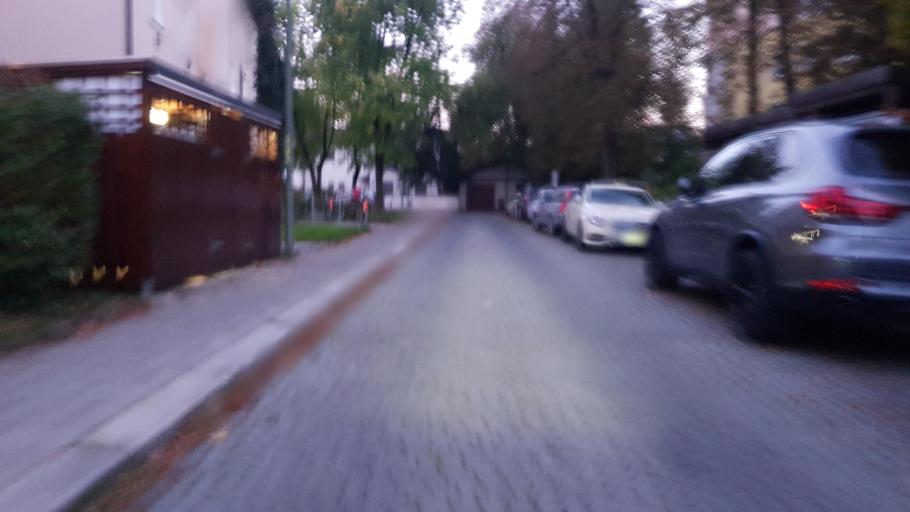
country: DE
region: Bavaria
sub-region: Upper Bavaria
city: Karlsfeld
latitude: 48.1764
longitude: 11.5080
